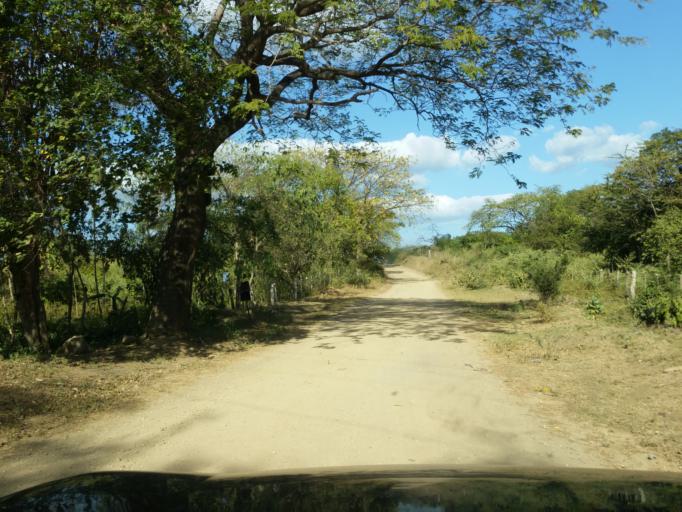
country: NI
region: Managua
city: Carlos Fonseca Amador
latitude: 11.9182
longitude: -86.5970
